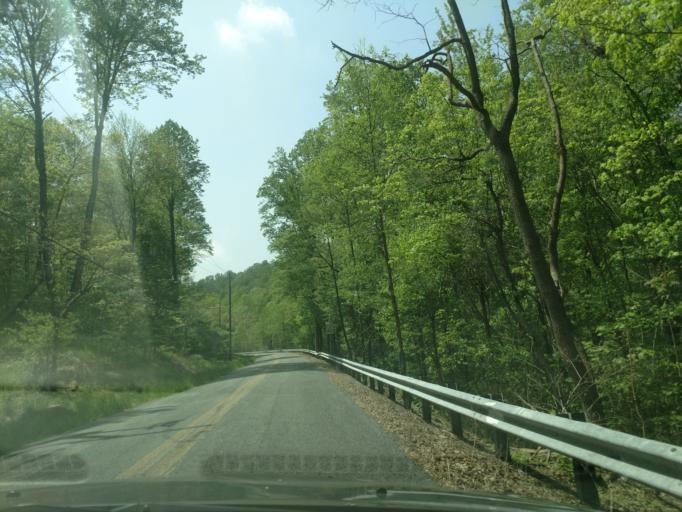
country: US
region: Pennsylvania
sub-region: Berks County
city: Birdsboro
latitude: 40.2385
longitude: -75.8342
